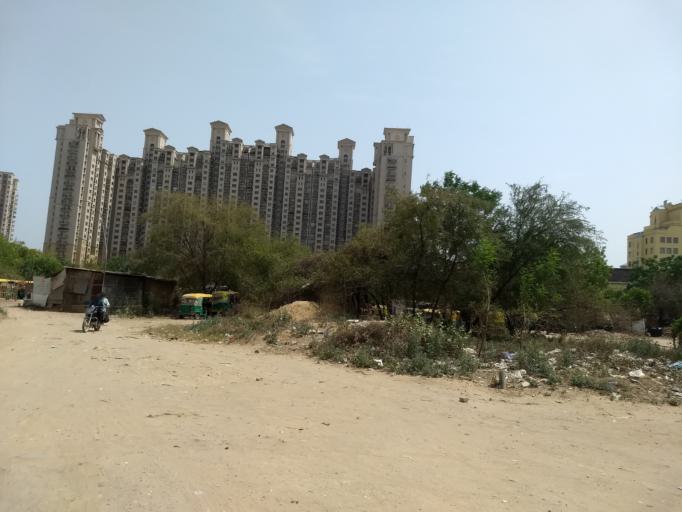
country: IN
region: Haryana
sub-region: Gurgaon
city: Gurgaon
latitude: 28.4698
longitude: 77.0843
